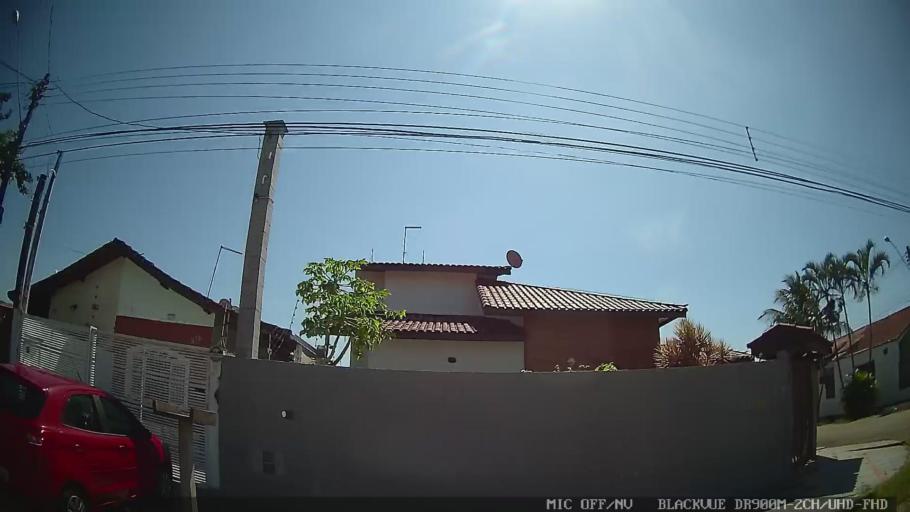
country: BR
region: Sao Paulo
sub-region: Peruibe
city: Peruibe
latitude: -24.2986
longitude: -46.9801
